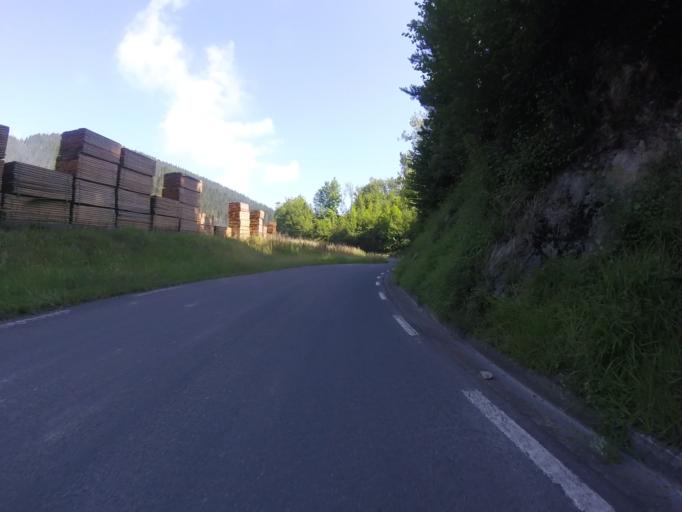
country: ES
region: Basque Country
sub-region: Provincia de Guipuzcoa
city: Ormaiztegui
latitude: 43.0634
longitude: -2.2376
